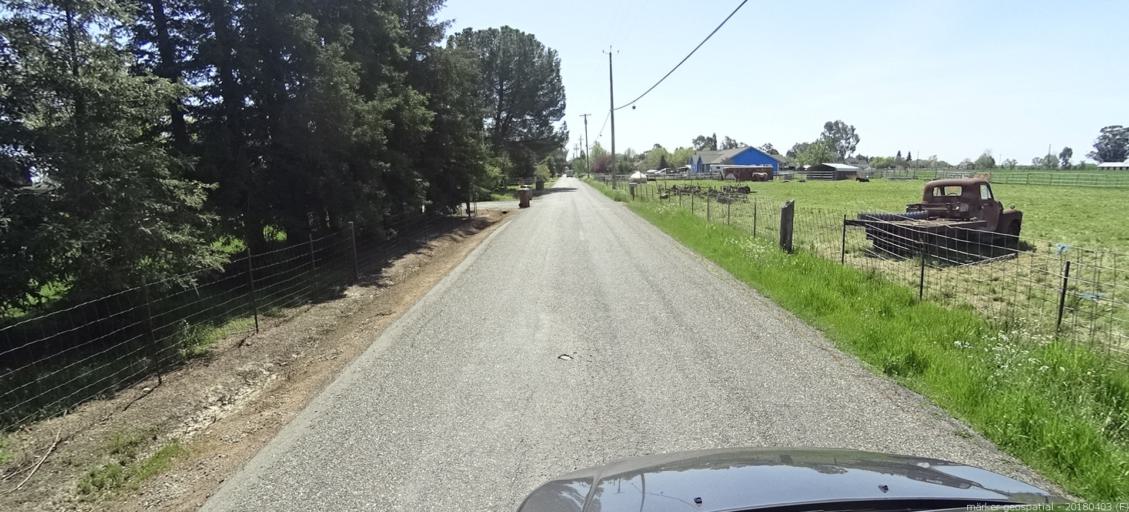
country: US
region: California
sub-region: Sacramento County
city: Wilton
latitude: 38.3933
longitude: -121.2698
